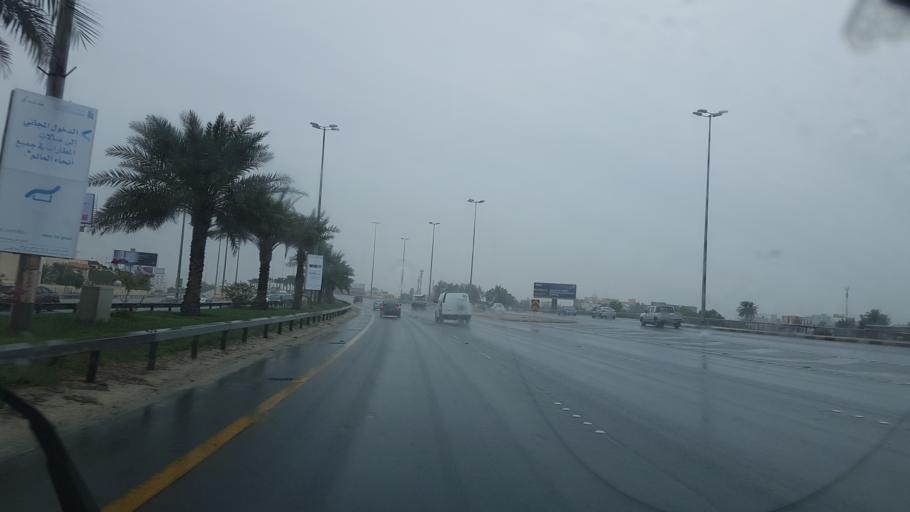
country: BH
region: Manama
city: Jidd Hafs
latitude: 26.2231
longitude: 50.5229
